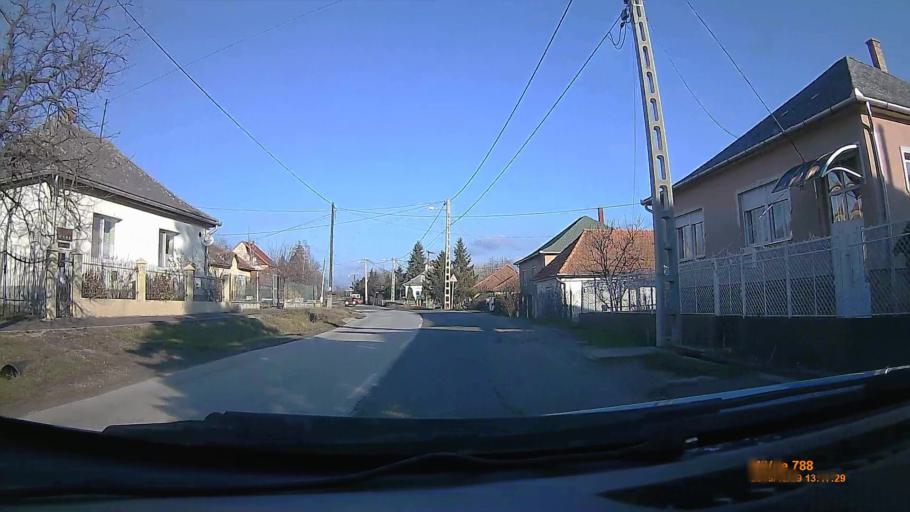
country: HU
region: Heves
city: Domoszlo
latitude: 47.8302
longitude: 20.1237
